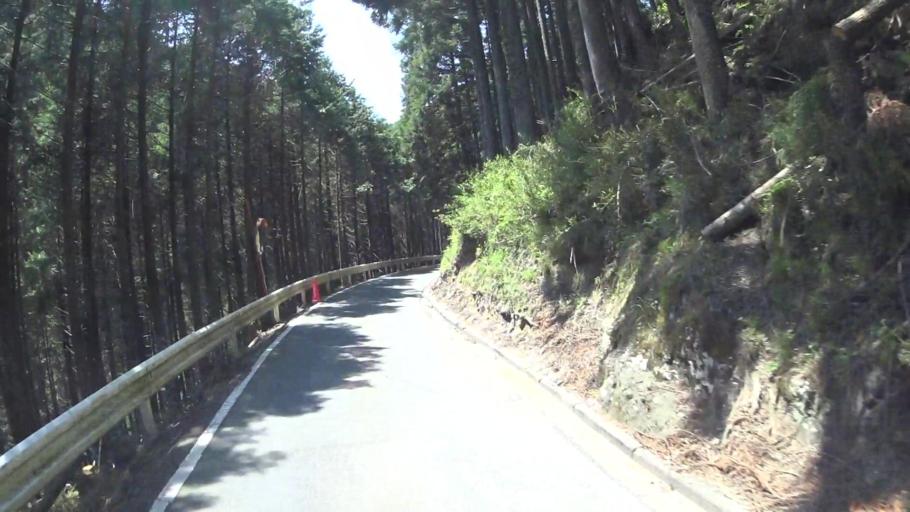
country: JP
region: Kyoto
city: Kameoka
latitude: 35.1309
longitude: 135.5830
